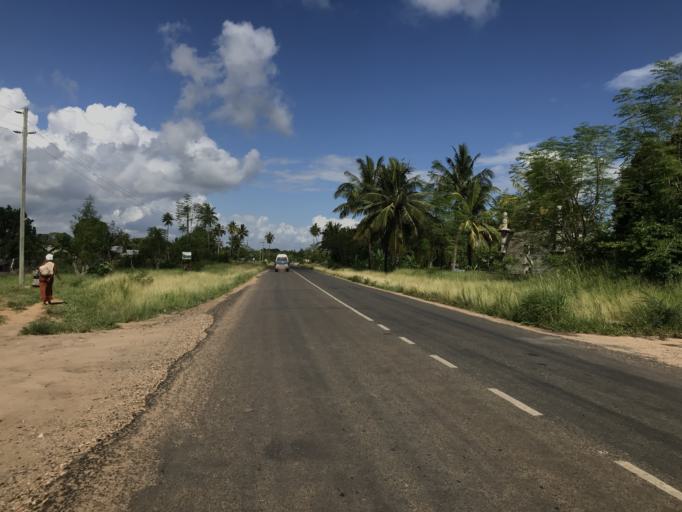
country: TZ
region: Dar es Salaam
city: Dar es Salaam
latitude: -6.8887
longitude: 39.4230
